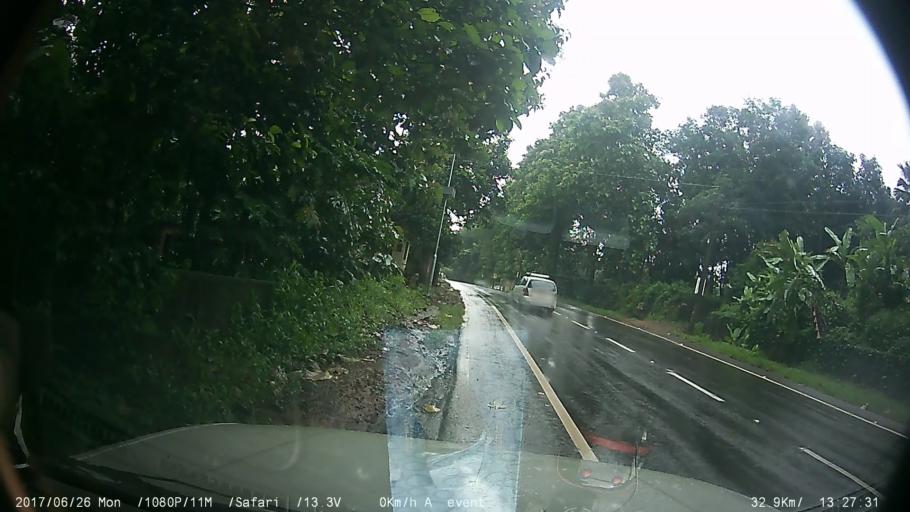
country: IN
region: Kerala
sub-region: Kottayam
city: Palackattumala
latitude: 9.6910
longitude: 76.5593
